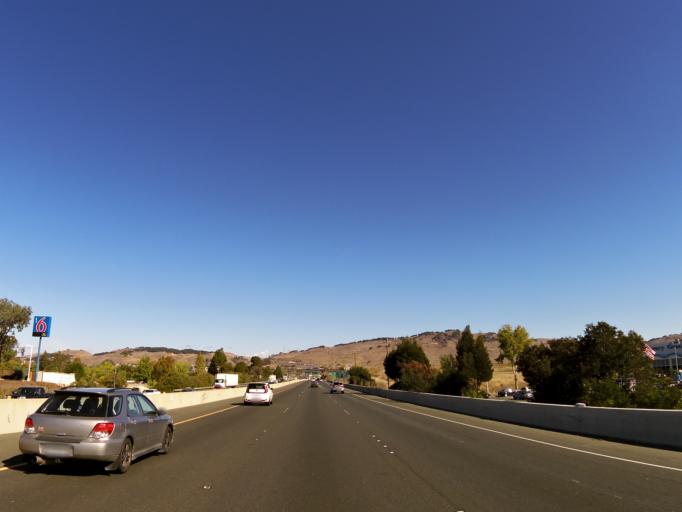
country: US
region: California
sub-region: Solano County
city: Vallejo
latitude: 38.1262
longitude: -122.2283
